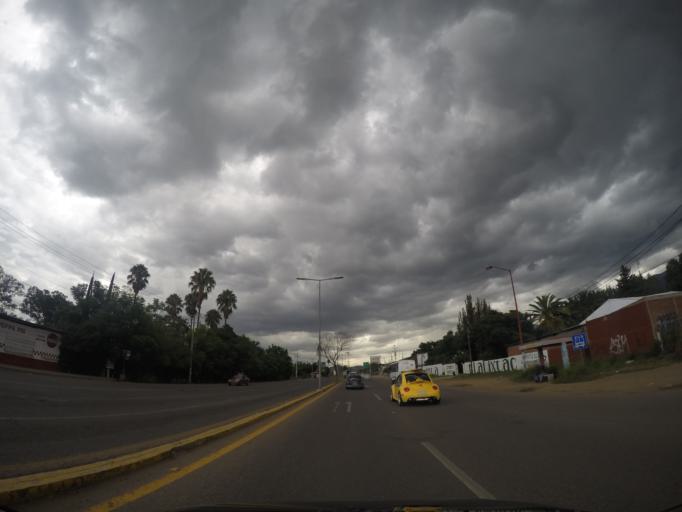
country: MX
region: Oaxaca
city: Tlalixtac de Cabrera
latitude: 17.0584
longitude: -96.6586
